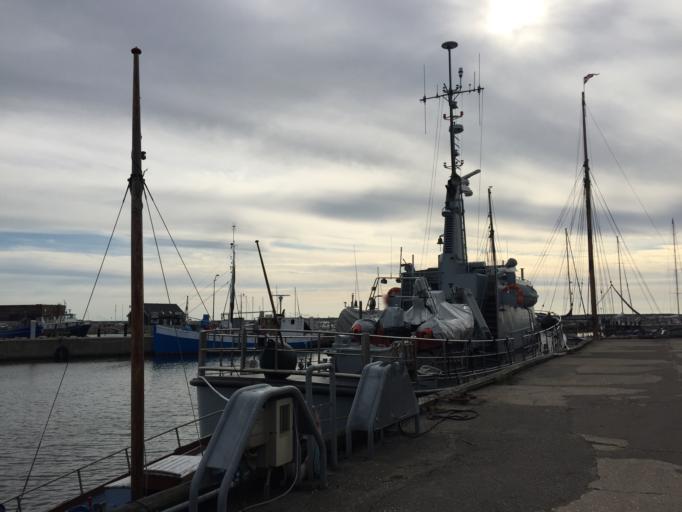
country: DK
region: Capital Region
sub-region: Halsnaes Kommune
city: Hundested
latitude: 55.9641
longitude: 11.8453
